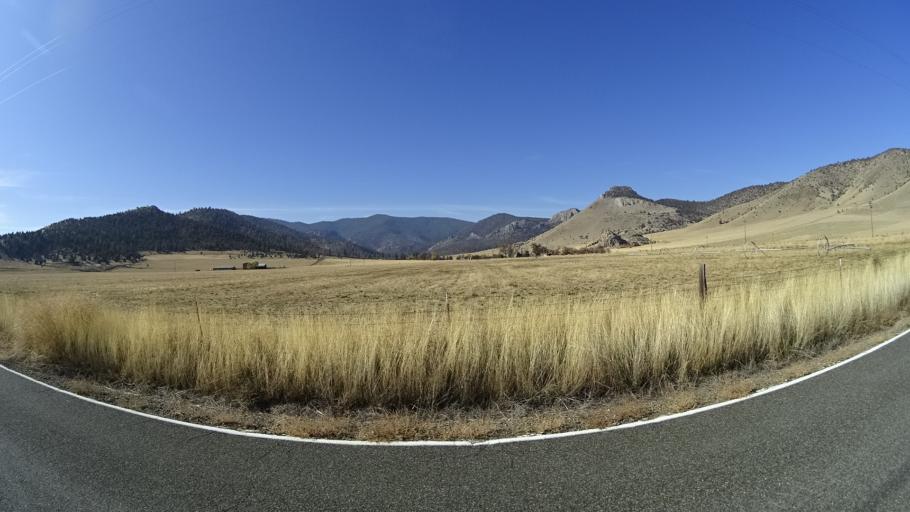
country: US
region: California
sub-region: Siskiyou County
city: Weed
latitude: 41.5021
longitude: -122.5498
